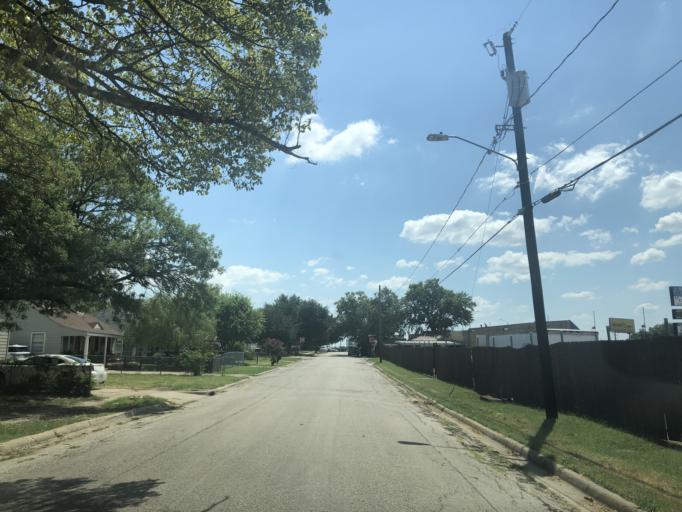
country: US
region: Texas
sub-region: Dallas County
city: Grand Prairie
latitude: 32.7407
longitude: -97.0320
